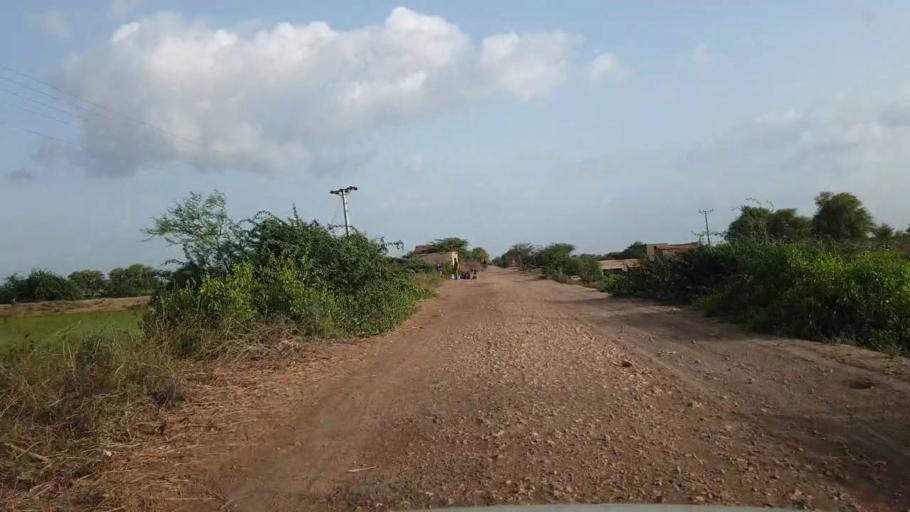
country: PK
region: Sindh
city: Kario
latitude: 24.8086
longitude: 68.6471
